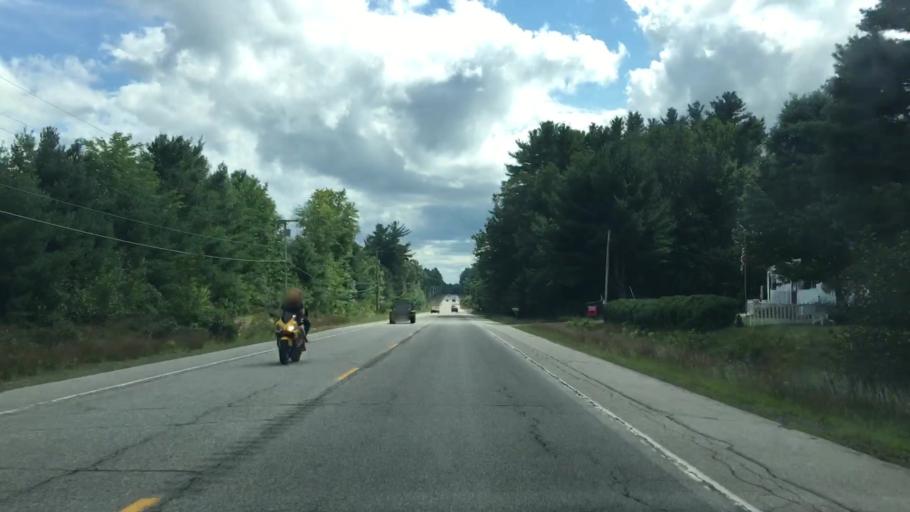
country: US
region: Maine
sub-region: York County
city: South Sanford
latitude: 43.3916
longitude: -70.7396
